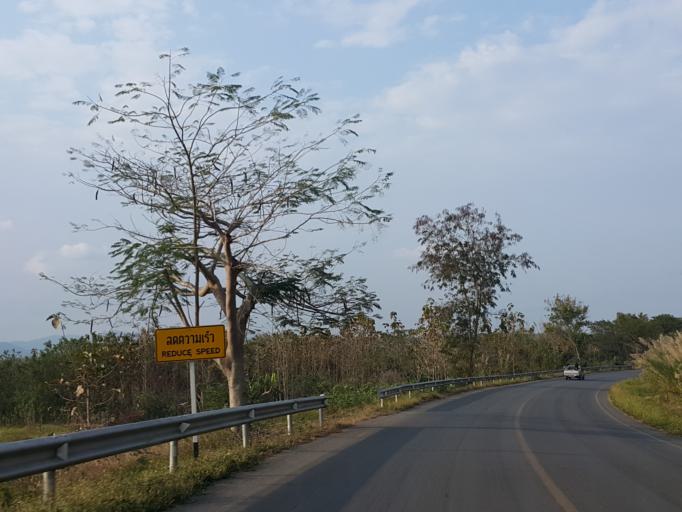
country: TH
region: Lampang
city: Hang Chat
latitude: 18.4423
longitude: 99.4504
